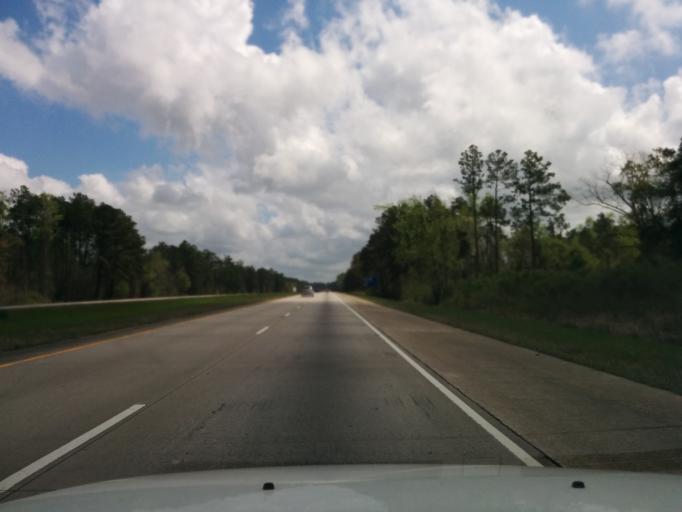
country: US
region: Georgia
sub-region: Bulloch County
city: Brooklet
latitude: 32.2662
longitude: -81.7389
